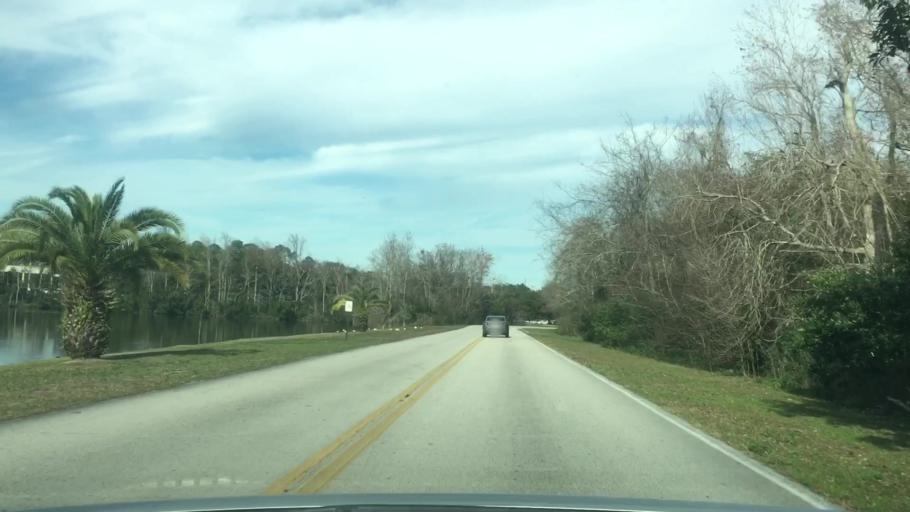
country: US
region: Florida
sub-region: Duval County
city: Neptune Beach
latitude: 30.2896
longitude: -81.5087
